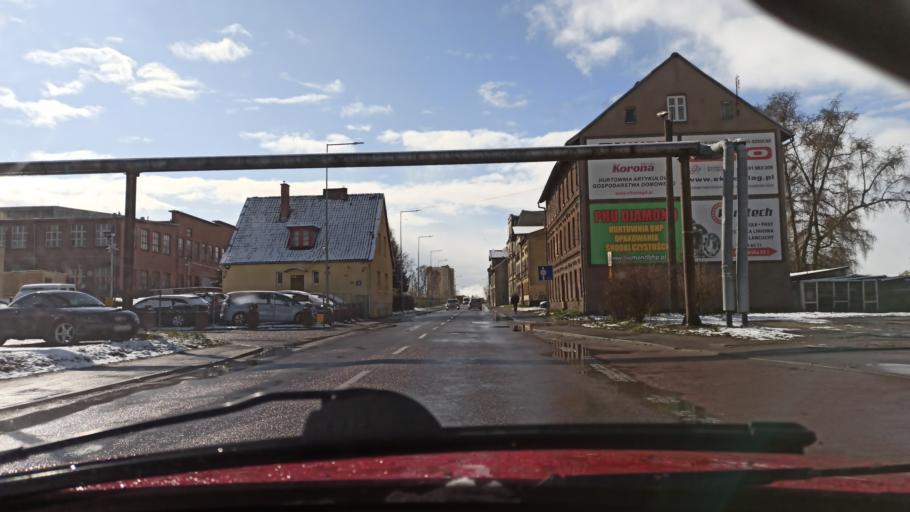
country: PL
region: Warmian-Masurian Voivodeship
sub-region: Powiat elblaski
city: Elblag
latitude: 54.1526
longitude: 19.4024
